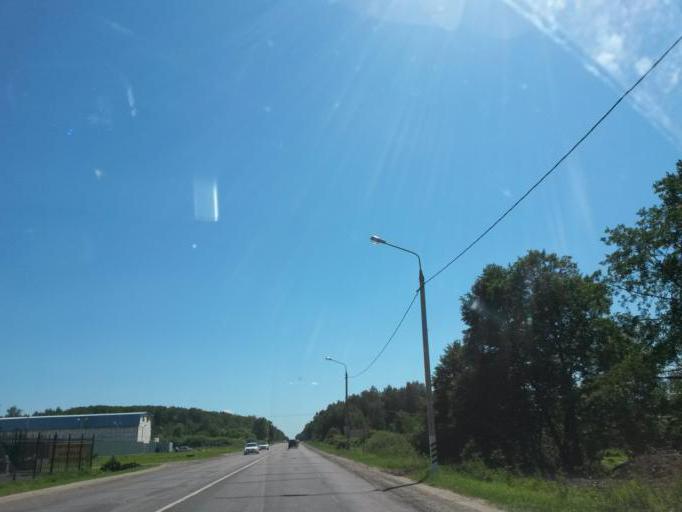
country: RU
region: Moskovskaya
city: Proletarskiy
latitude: 55.0653
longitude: 37.4361
